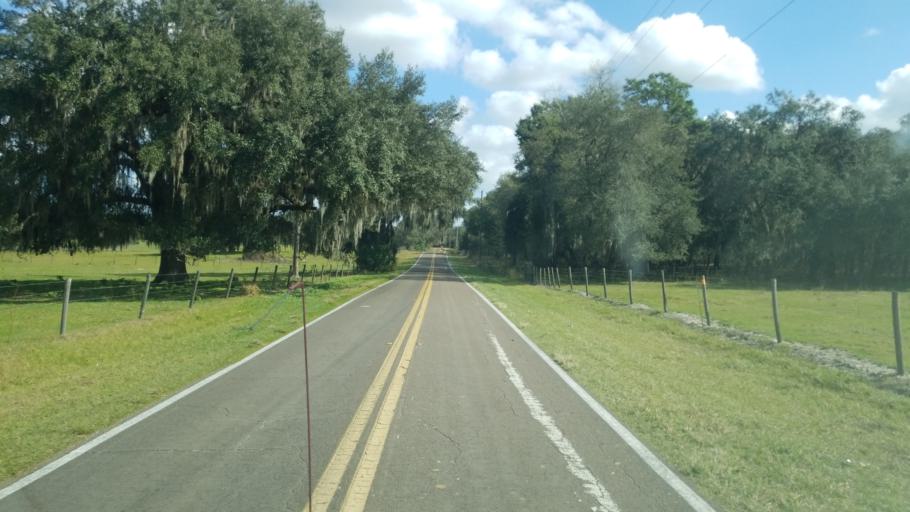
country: US
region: Florida
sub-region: Citrus County
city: Floral City
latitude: 28.7548
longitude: -82.2491
